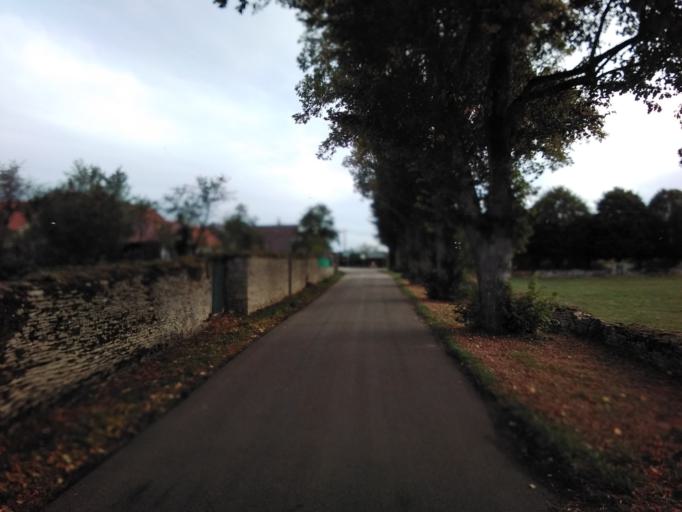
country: FR
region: Bourgogne
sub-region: Departement de l'Yonne
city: Ravieres
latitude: 47.7793
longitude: 4.3525
